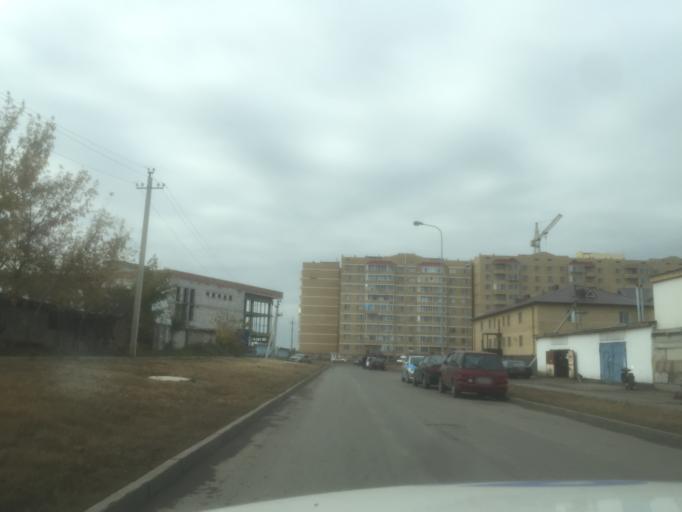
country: KZ
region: Astana Qalasy
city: Astana
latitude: 51.1733
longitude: 71.3737
